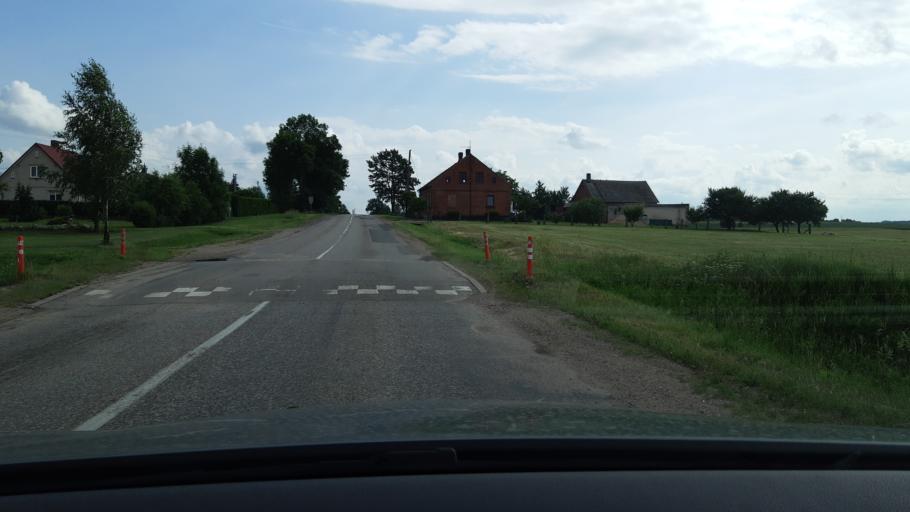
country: LT
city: Kybartai
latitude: 54.6120
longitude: 22.7440
